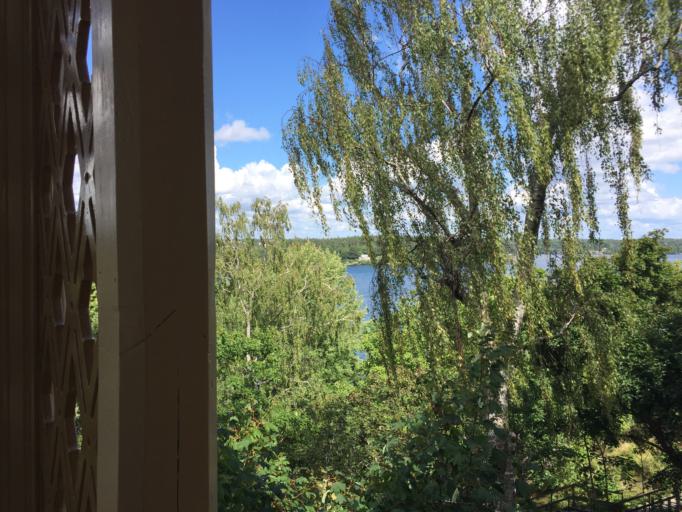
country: SE
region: Stockholm
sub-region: Huddinge Kommun
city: Segeltorp
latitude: 59.3014
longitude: 17.9361
